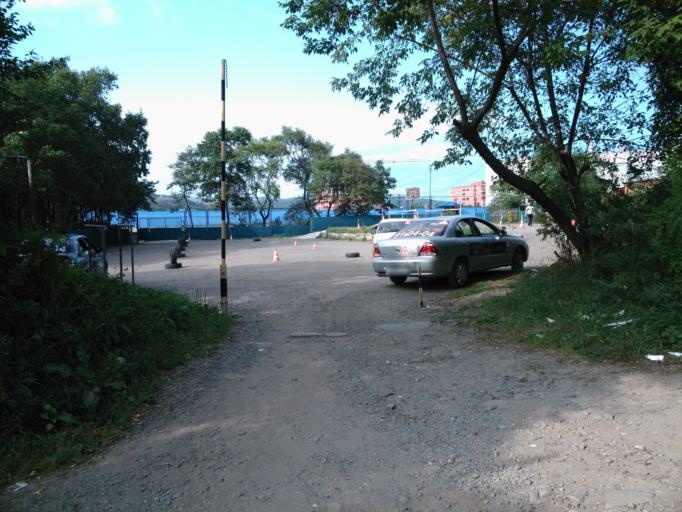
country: RU
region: Primorskiy
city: Vladivostok
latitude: 43.0933
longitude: 131.9600
